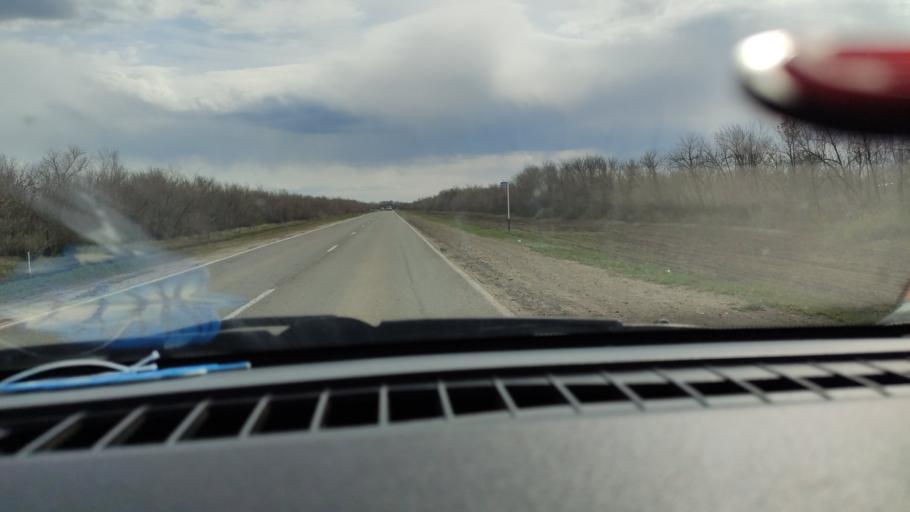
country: RU
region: Saratov
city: Privolzhskiy
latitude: 51.3583
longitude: 46.0440
